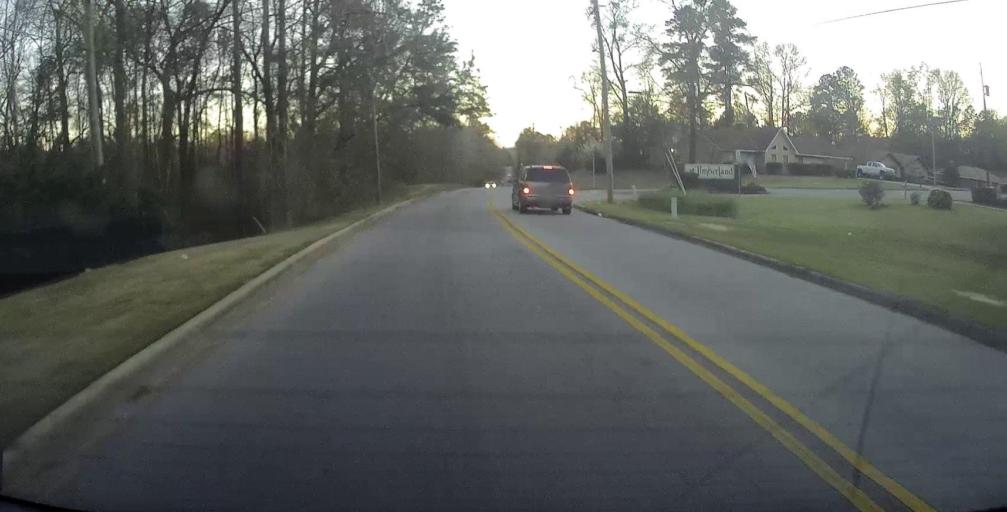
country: US
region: Alabama
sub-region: Russell County
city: Phenix City
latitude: 32.4924
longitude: -85.0184
